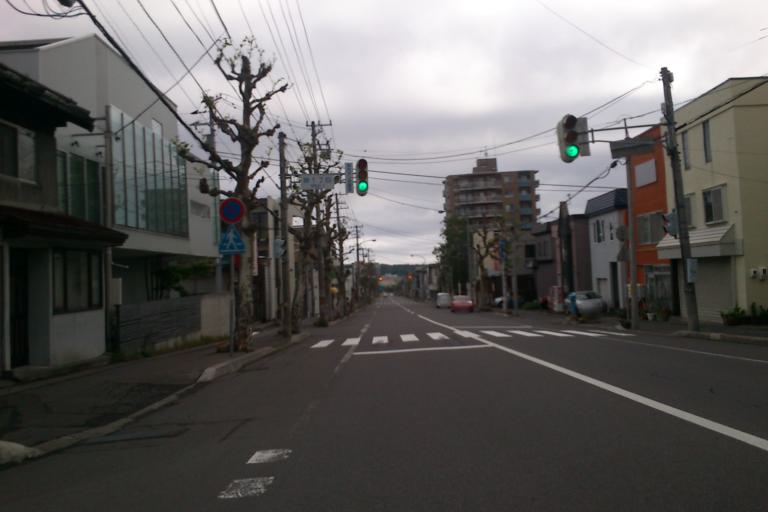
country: JP
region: Hokkaido
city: Otaru
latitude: 43.1882
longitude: 140.9888
